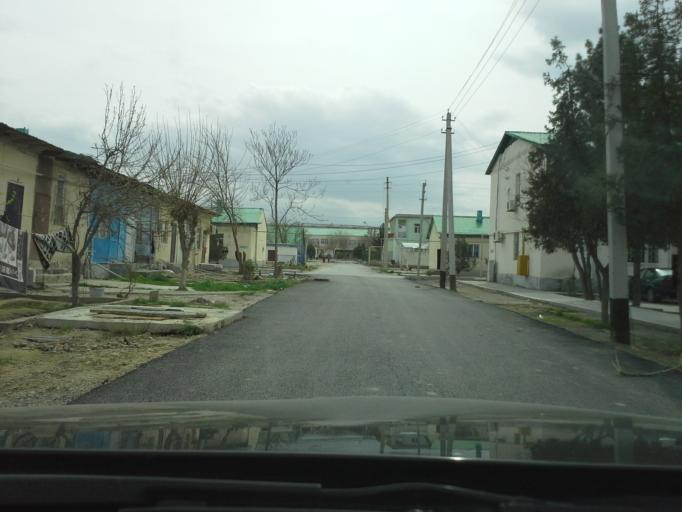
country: TM
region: Ahal
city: Abadan
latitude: 38.0578
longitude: 58.1543
